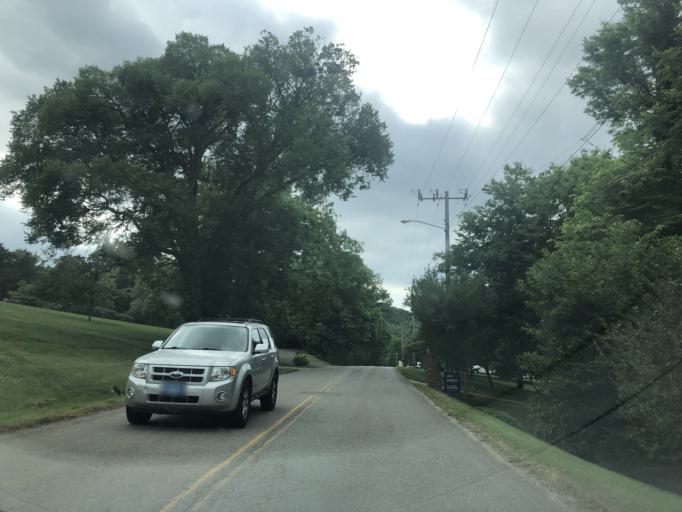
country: US
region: Tennessee
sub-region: Davidson County
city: Forest Hills
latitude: 36.0787
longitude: -86.8183
